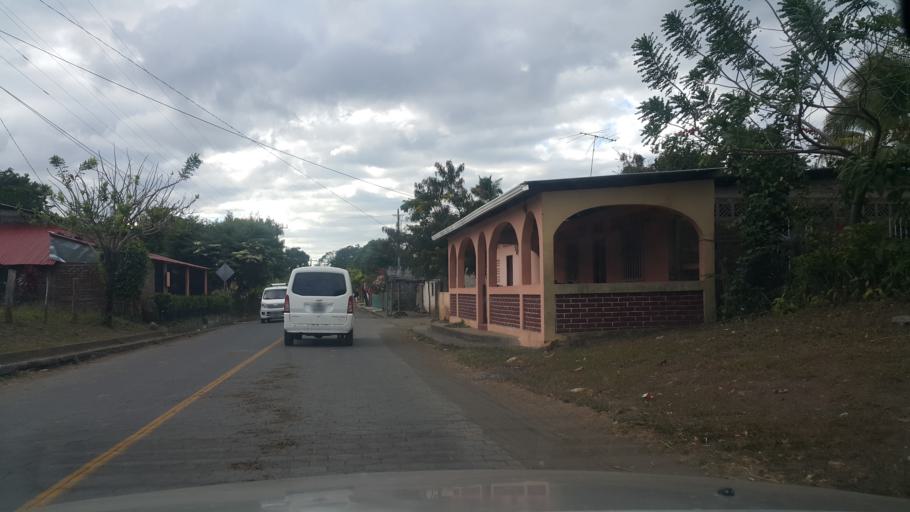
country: NI
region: Rivas
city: Moyogalpa
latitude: 11.4962
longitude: -85.6920
